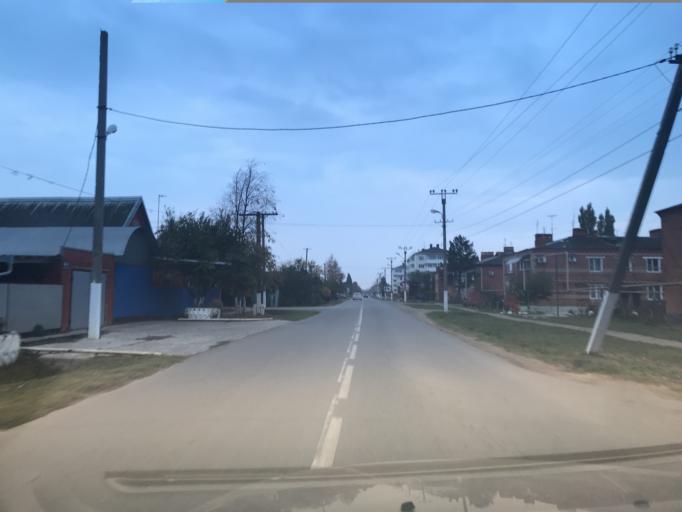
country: RU
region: Krasnodarskiy
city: Sovkhoznyy
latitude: 45.2725
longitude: 38.1034
